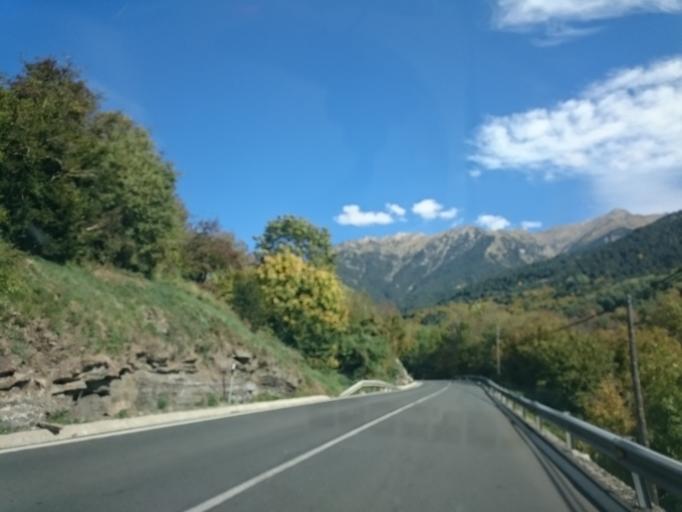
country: ES
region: Aragon
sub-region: Provincia de Huesca
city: Bonansa
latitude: 42.5504
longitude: 0.7454
